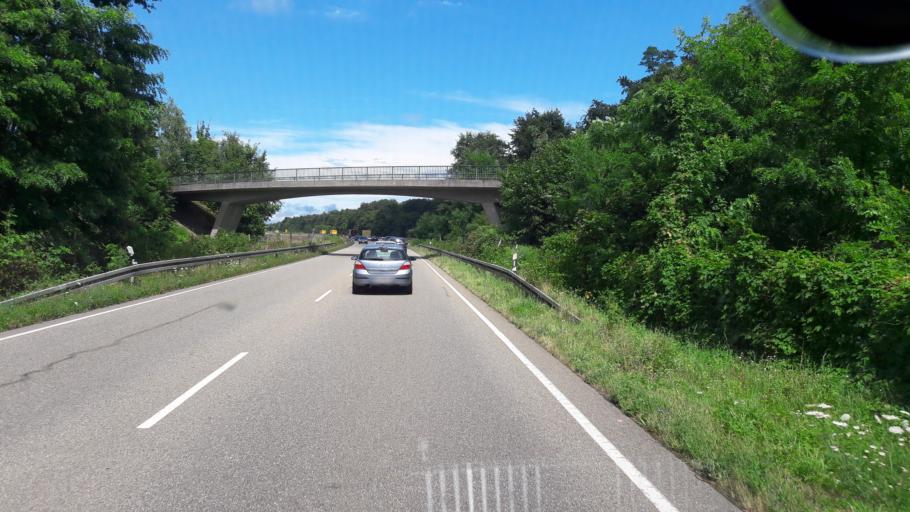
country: DE
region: Baden-Wuerttemberg
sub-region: Karlsruhe Region
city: Linkenheim-Hochstetten
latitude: 49.1099
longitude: 8.4260
